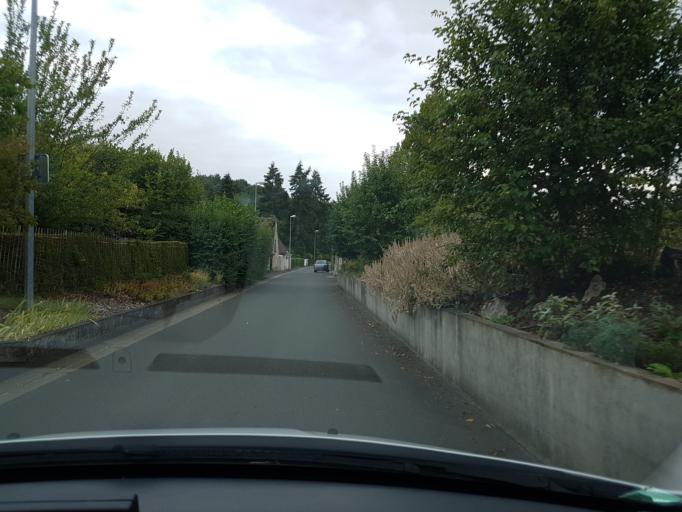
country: FR
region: Centre
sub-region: Departement d'Indre-et-Loire
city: Saint-Avertin
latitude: 47.3640
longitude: 0.7590
